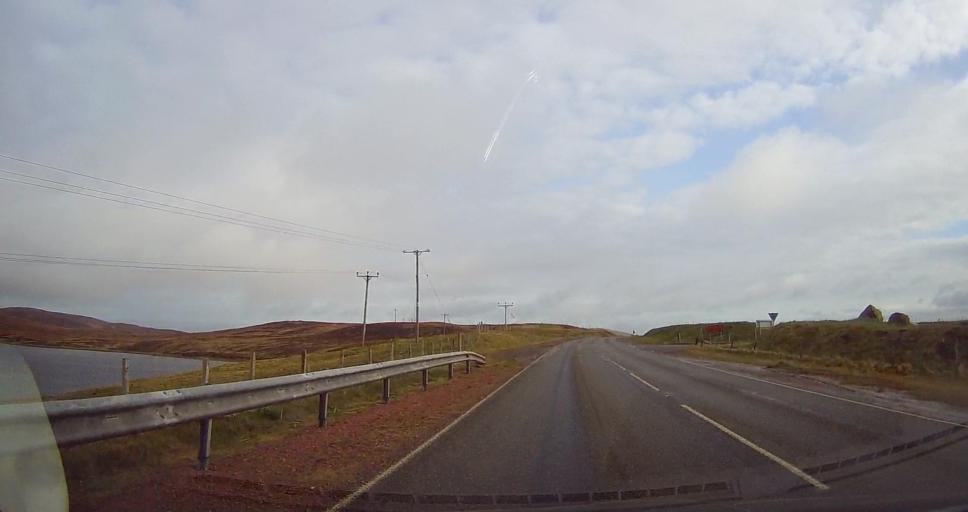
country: GB
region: Scotland
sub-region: Shetland Islands
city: Lerwick
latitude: 60.1136
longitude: -1.2188
